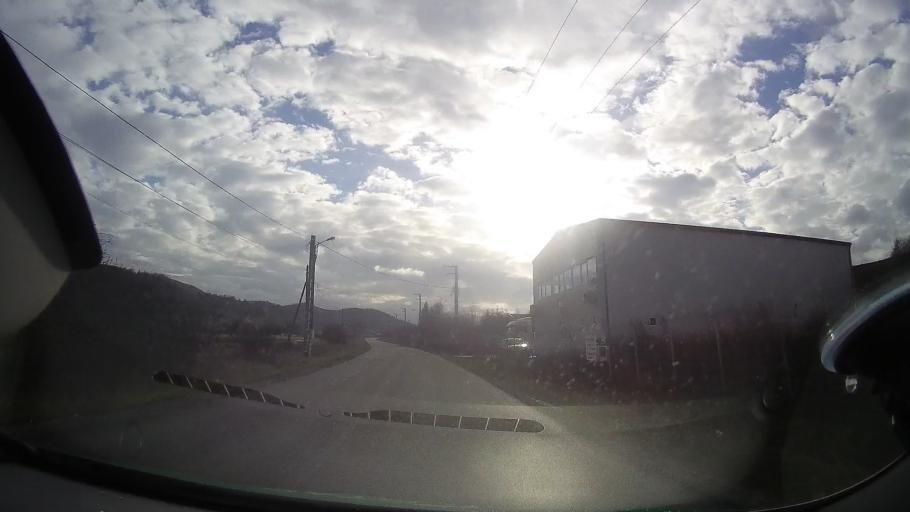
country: RO
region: Cluj
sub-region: Comuna Floresti
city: Luna de Sus
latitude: 46.7197
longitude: 23.4241
